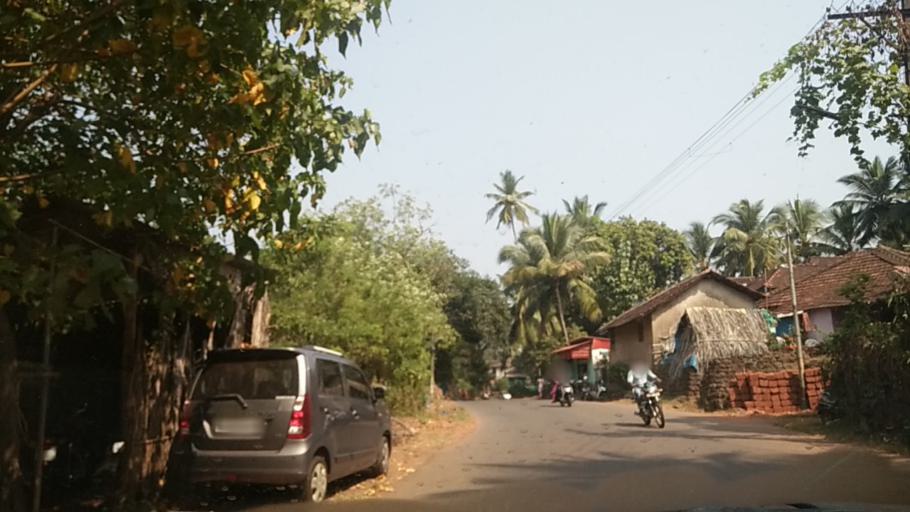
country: IN
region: Goa
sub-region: South Goa
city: Cavelossim
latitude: 15.1497
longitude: 73.9611
